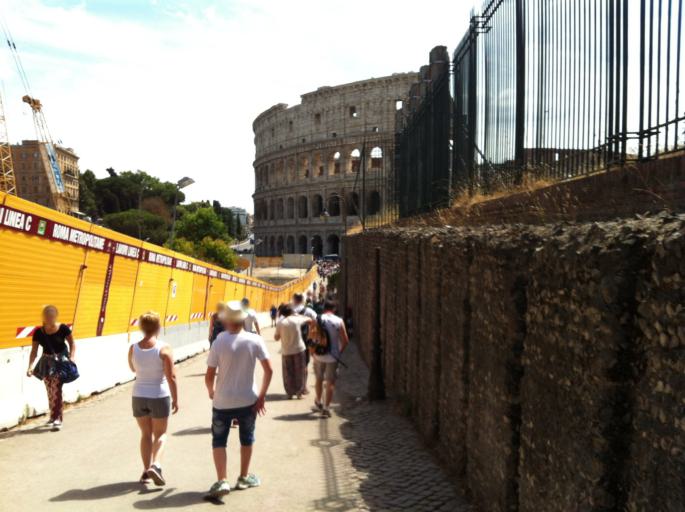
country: IT
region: Latium
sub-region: Citta metropolitana di Roma Capitale
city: Rome
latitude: 41.8914
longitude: 12.4897
